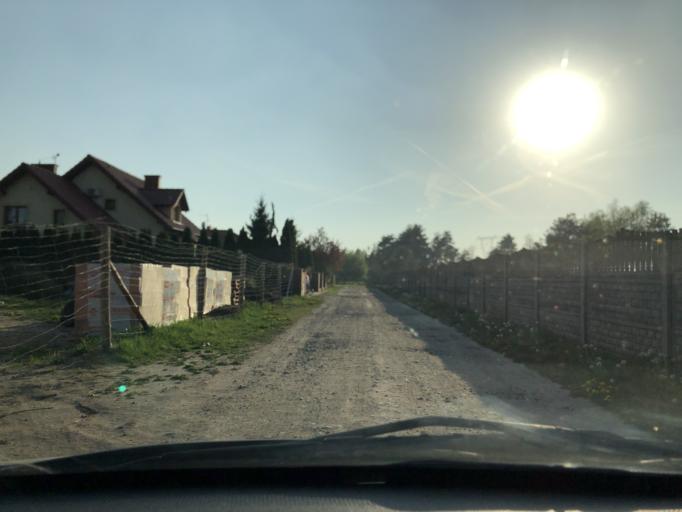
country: PL
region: Greater Poland Voivodeship
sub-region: Powiat poznanski
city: Baranowo
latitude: 52.3944
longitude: 16.7488
